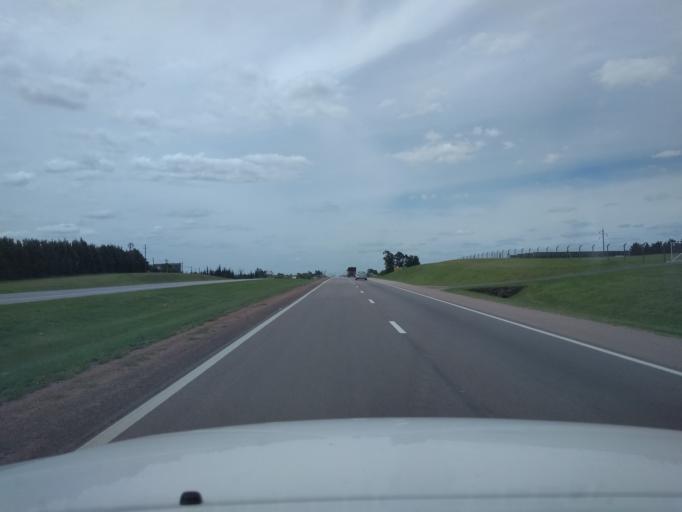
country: UY
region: Canelones
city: Las Piedras
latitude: -34.7342
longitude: -56.2495
